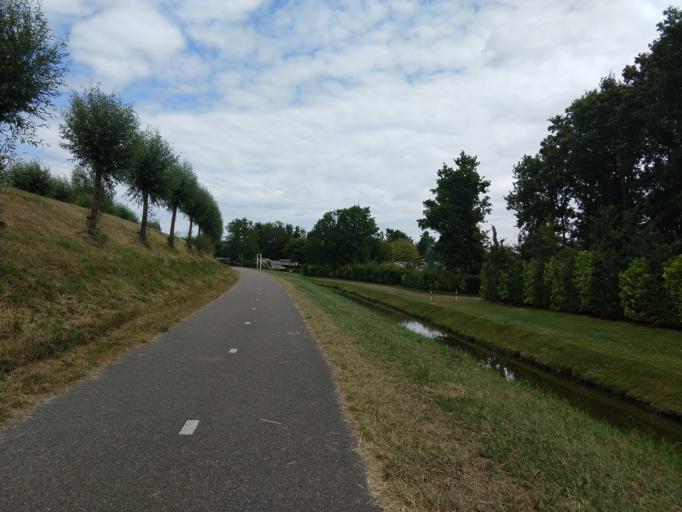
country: NL
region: Zeeland
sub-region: Gemeente Goes
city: Goes
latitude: 51.5438
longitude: 3.8075
